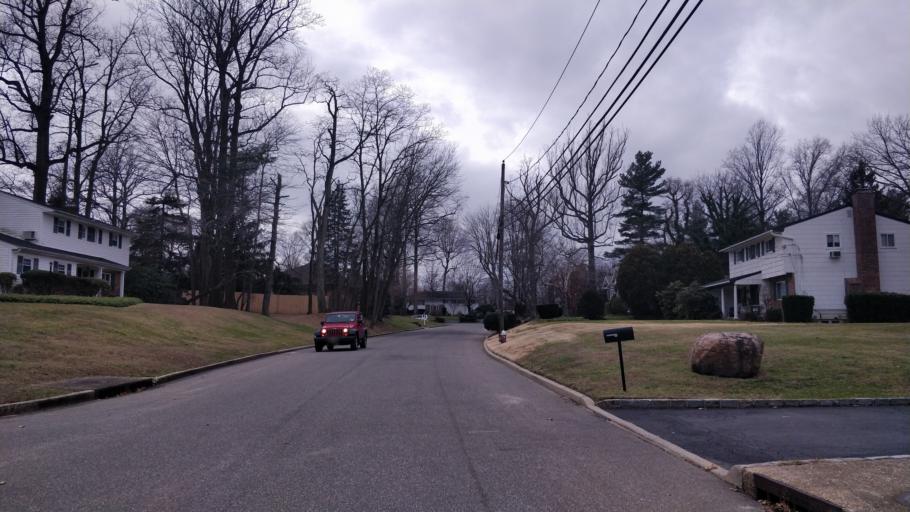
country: US
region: New York
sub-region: Nassau County
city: Lattingtown
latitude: 40.8828
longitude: -73.6212
